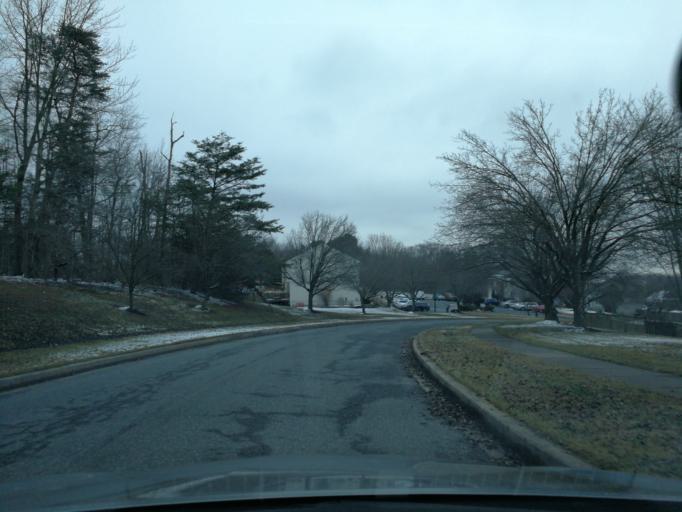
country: US
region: Maryland
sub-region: Harford County
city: Bel Air South
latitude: 39.4729
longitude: -76.2954
